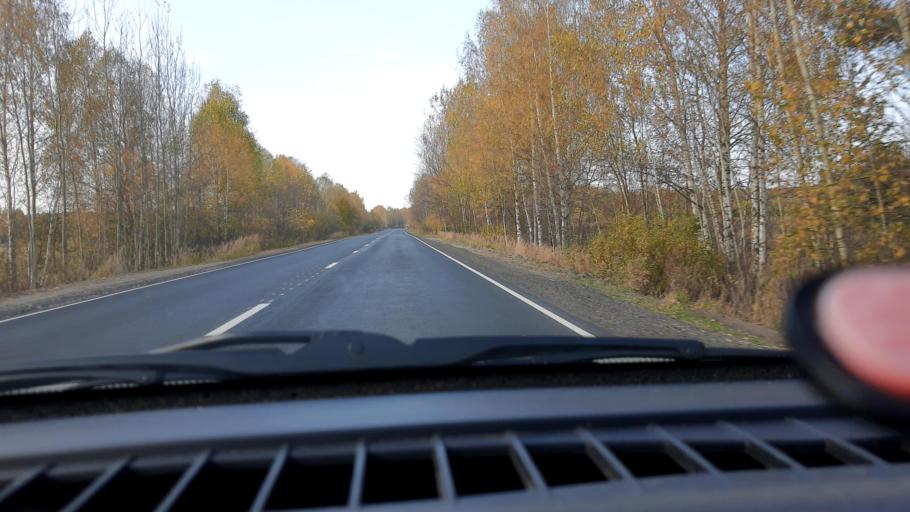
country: RU
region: Nizjnij Novgorod
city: Lukino
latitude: 56.5383
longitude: 43.7760
